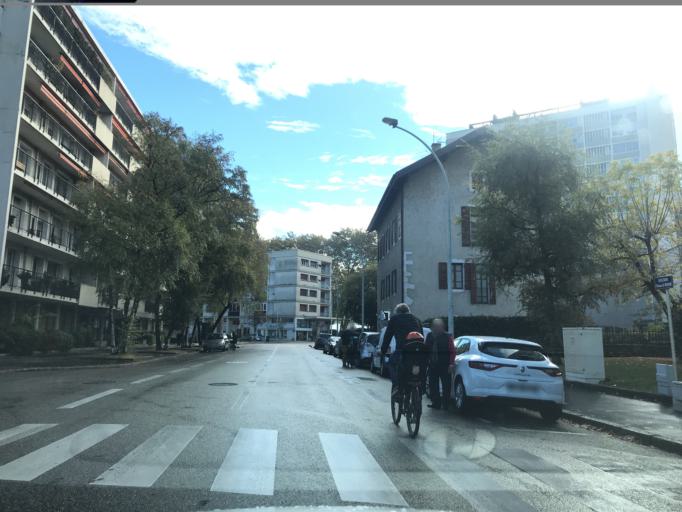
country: FR
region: Rhone-Alpes
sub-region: Departement de la Haute-Savoie
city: Annecy-le-Vieux
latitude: 45.9045
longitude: 6.1343
